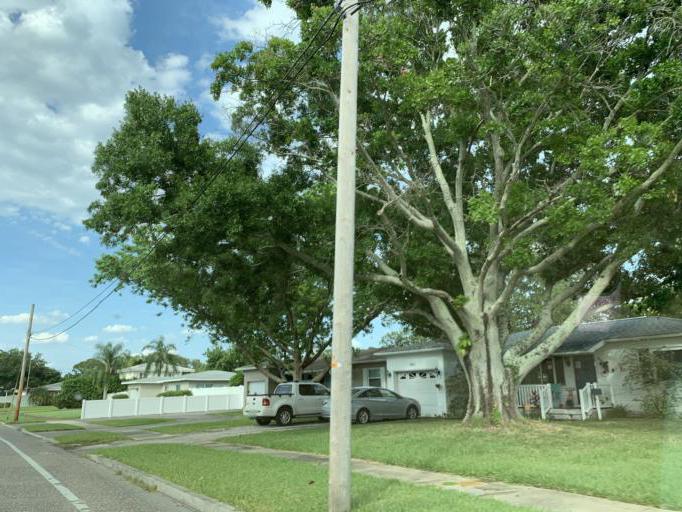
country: US
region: Florida
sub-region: Pinellas County
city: Gandy
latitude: 27.8067
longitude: -82.6039
